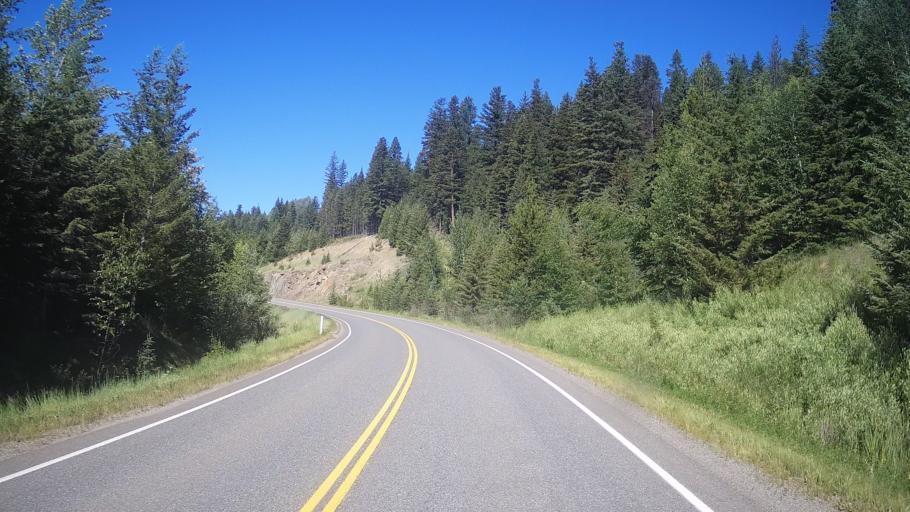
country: CA
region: British Columbia
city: Kamloops
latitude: 51.4736
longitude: -120.5428
